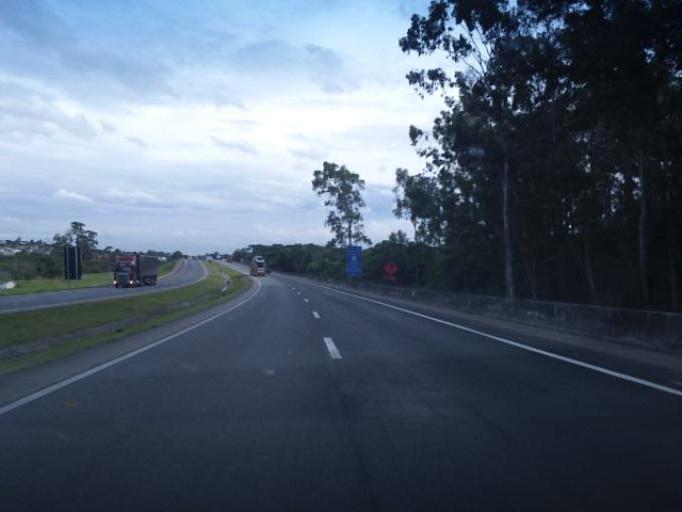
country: BR
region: Parana
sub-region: Piraquara
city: Piraquara
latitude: -25.4448
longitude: -49.0921
